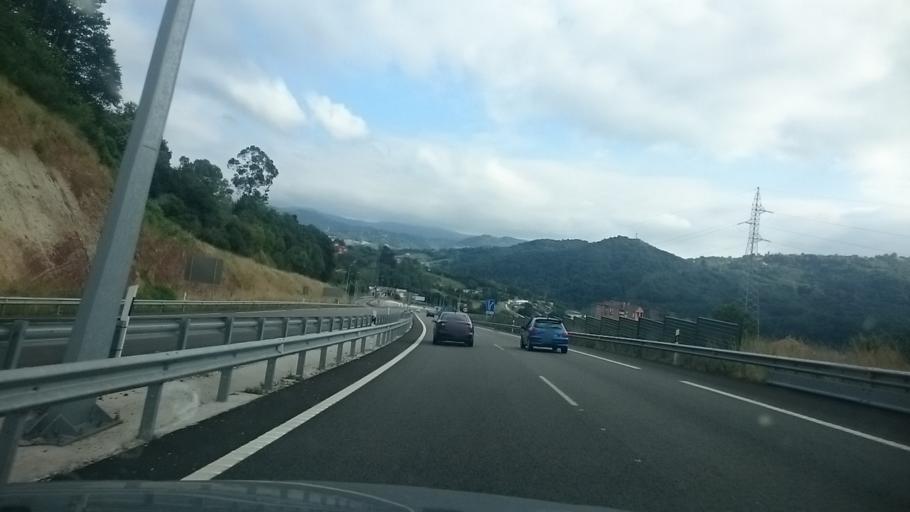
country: ES
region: Asturias
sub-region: Province of Asturias
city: Sama
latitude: 43.3319
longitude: -5.7138
